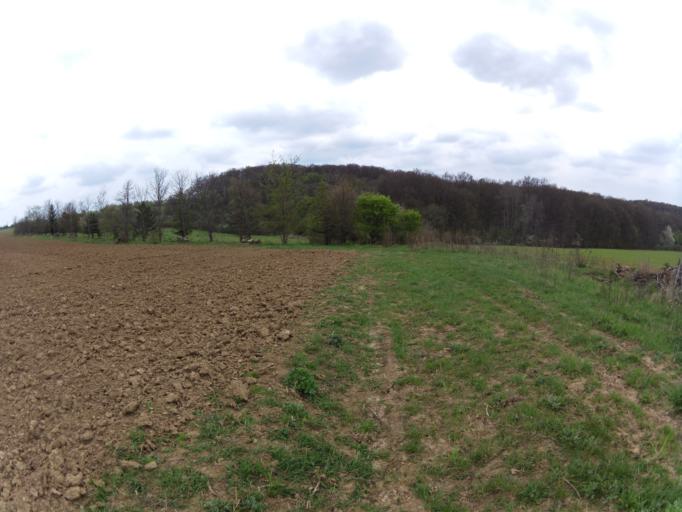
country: DE
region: Bavaria
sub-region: Regierungsbezirk Unterfranken
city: Greussenheim
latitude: 49.8285
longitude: 9.7893
